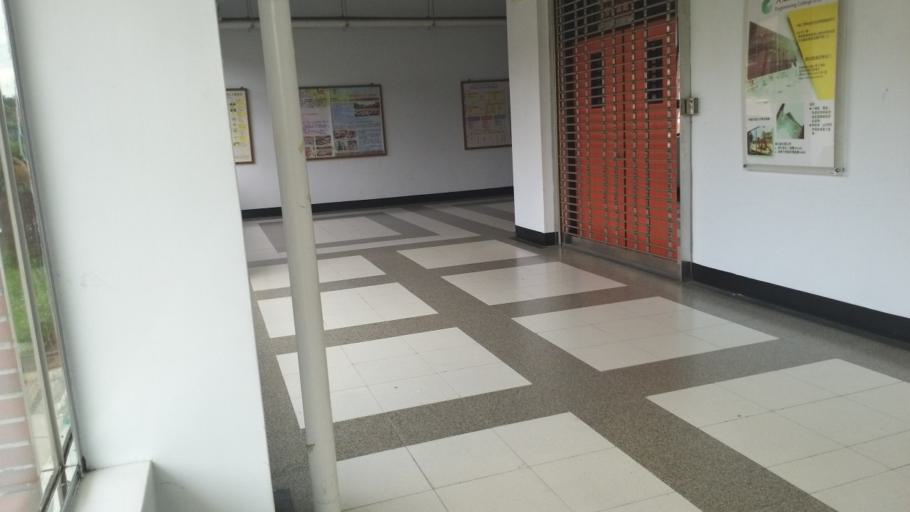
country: TW
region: Taiwan
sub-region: Changhua
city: Chang-hua
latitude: 24.0001
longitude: 120.5982
